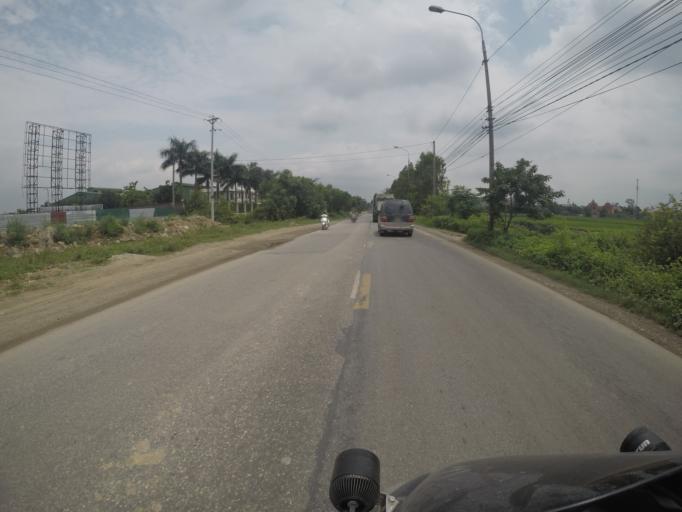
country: VN
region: Ha Noi
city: Soc Son
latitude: 21.2193
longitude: 105.8489
